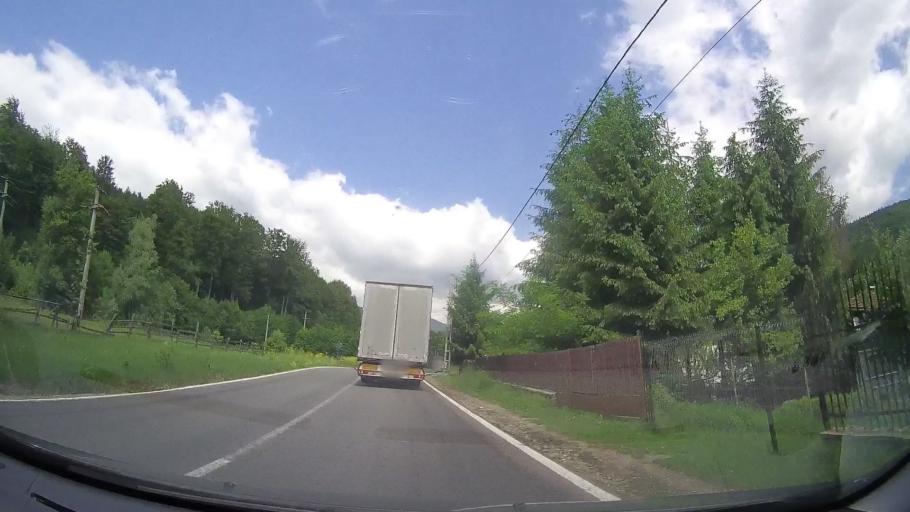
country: RO
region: Prahova
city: Maneciu
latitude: 45.3600
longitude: 25.9416
